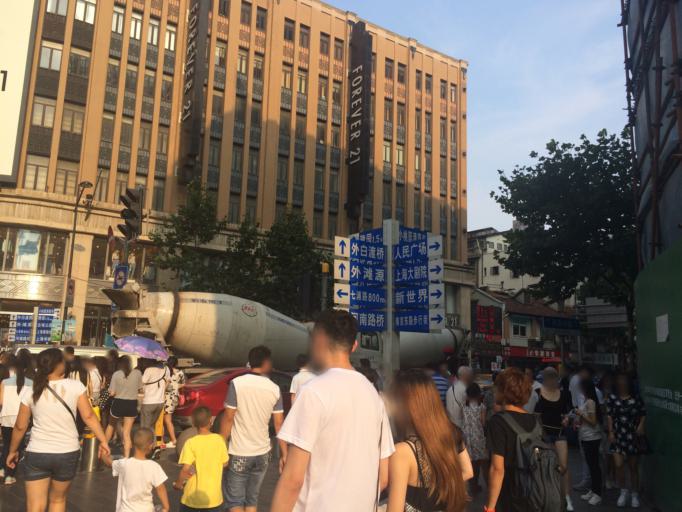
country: CN
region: Shanghai Shi
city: Hongkou
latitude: 31.2394
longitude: 121.4800
